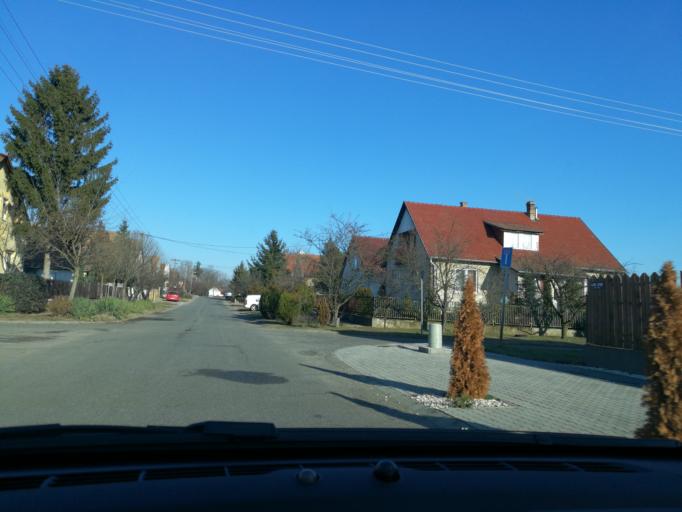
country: HU
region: Szabolcs-Szatmar-Bereg
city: Nyiregyhaza
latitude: 47.9278
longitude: 21.7585
